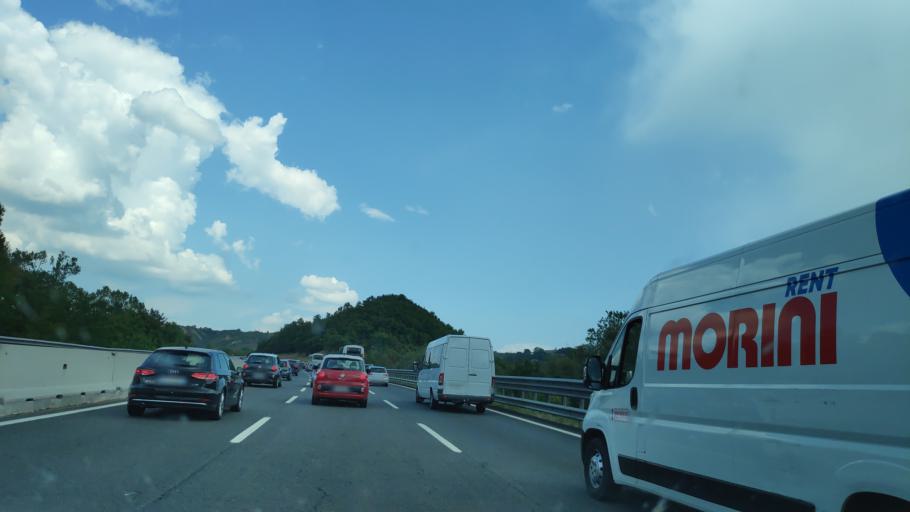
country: IT
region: Umbria
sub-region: Provincia di Terni
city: Ficulle
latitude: 42.8231
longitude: 12.0395
